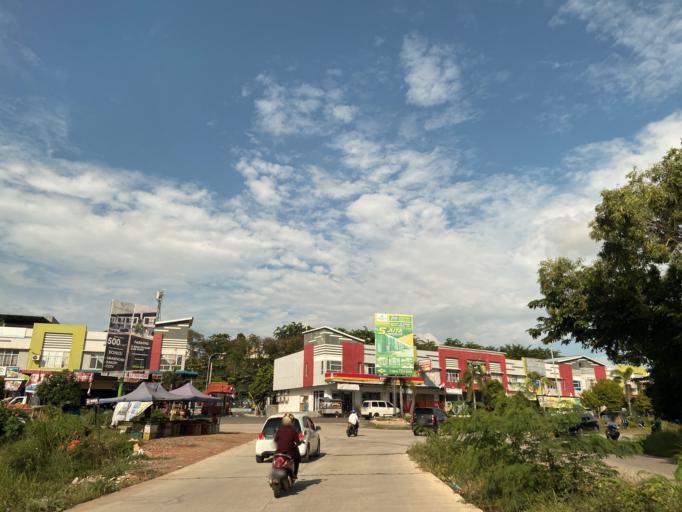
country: SG
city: Singapore
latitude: 1.1118
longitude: 104.0768
